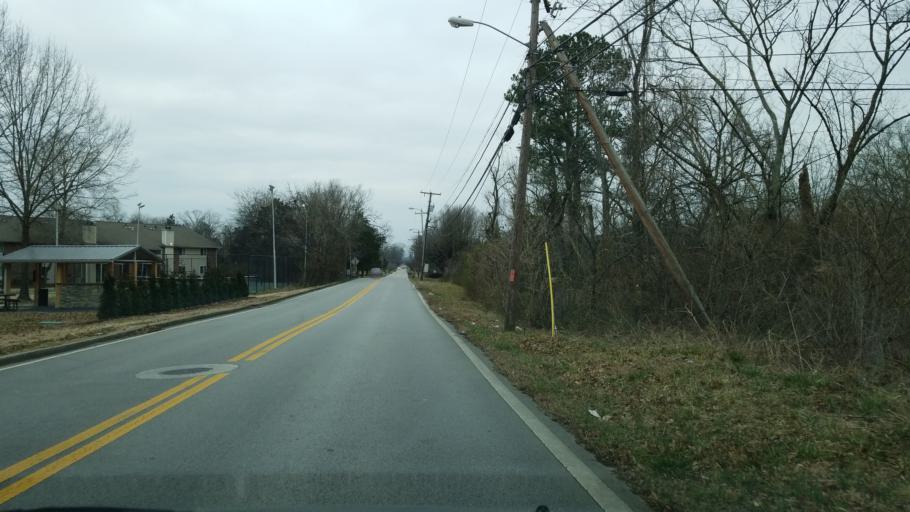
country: US
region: Tennessee
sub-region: Hamilton County
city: East Brainerd
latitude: 35.0527
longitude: -85.1511
